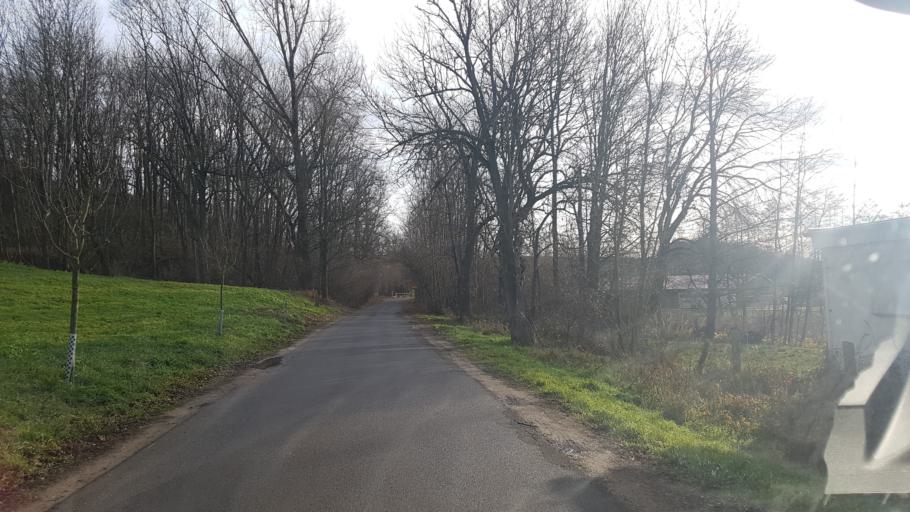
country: DE
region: Saxony
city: Ostrau
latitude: 51.1887
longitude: 13.1704
